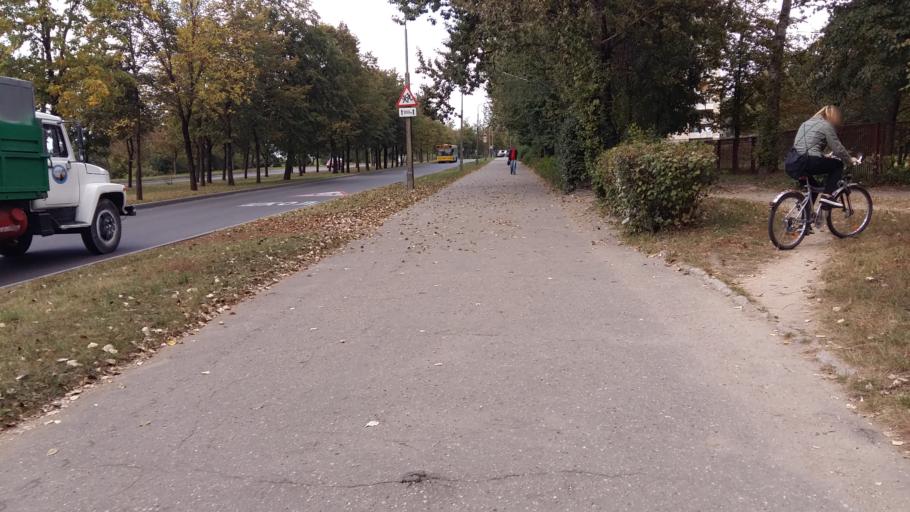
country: BY
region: Grodnenskaya
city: Hrodna
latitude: 53.7004
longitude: 23.7989
